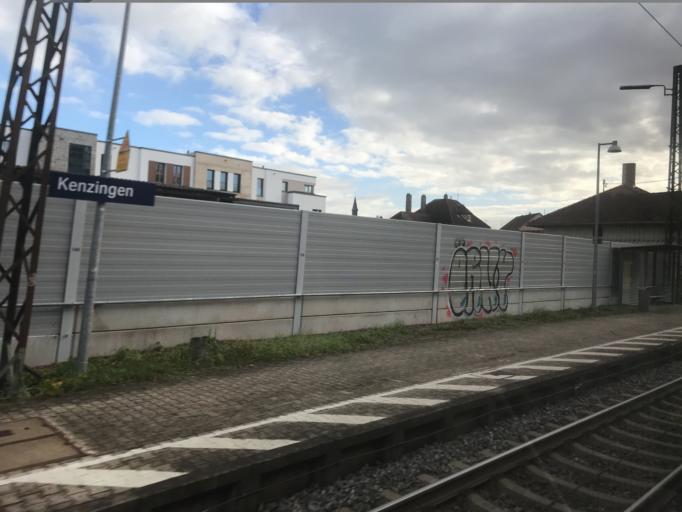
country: DE
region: Baden-Wuerttemberg
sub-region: Freiburg Region
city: Kenzingen
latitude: 48.1956
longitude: 7.7644
